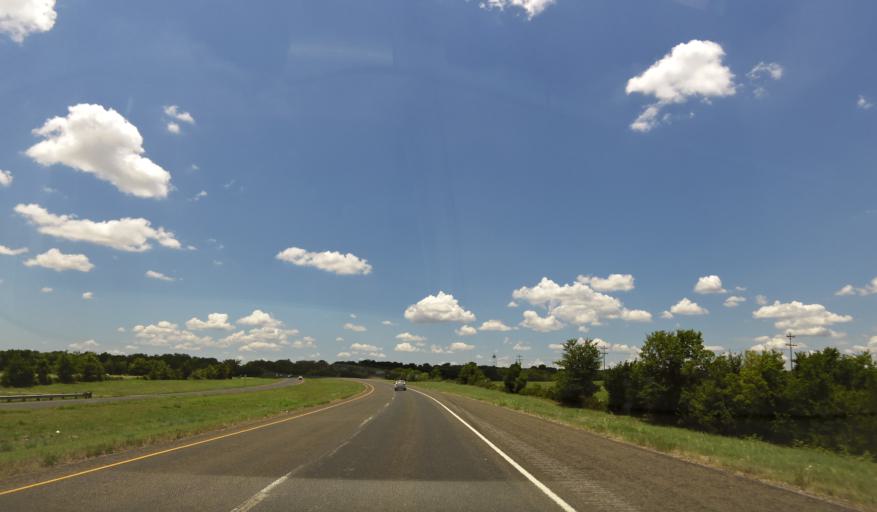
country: US
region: Texas
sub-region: Burleson County
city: Somerville
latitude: 30.1838
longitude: -96.5849
